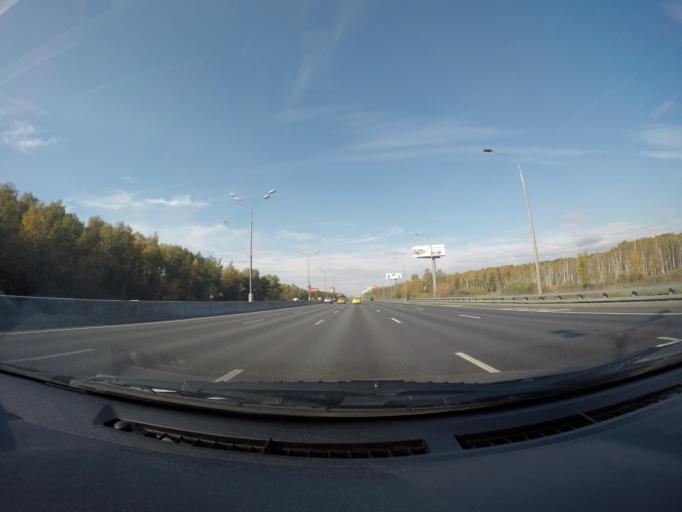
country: RU
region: Moskovskaya
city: Druzhba
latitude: 55.8692
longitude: 37.7520
